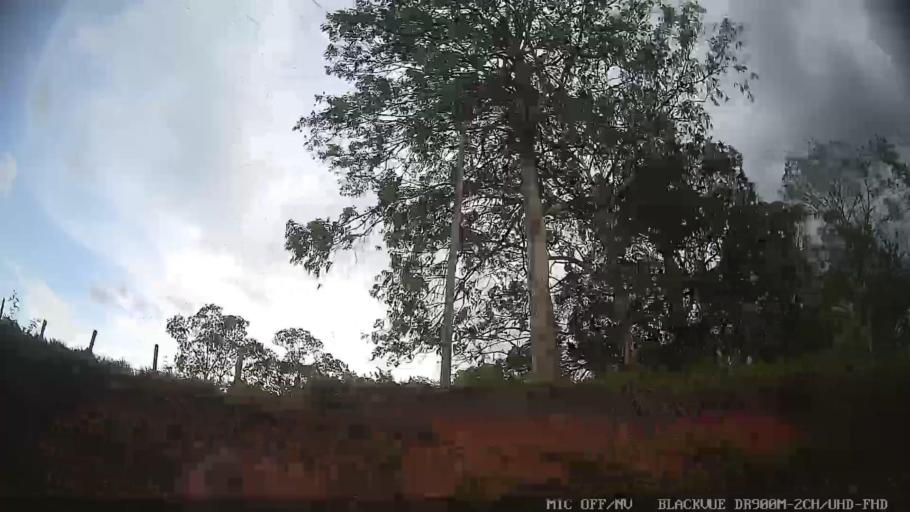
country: BR
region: Sao Paulo
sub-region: Itatiba
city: Itatiba
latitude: -22.9424
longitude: -46.8090
